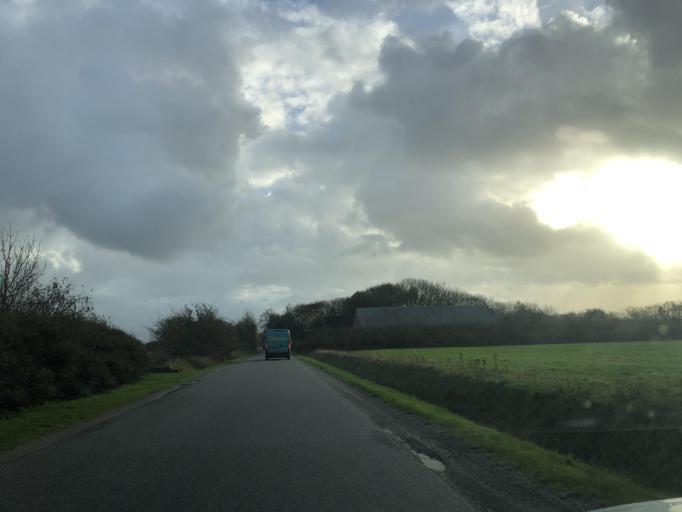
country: DK
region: South Denmark
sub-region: Esbjerg Kommune
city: Bramming
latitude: 55.4141
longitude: 8.7054
